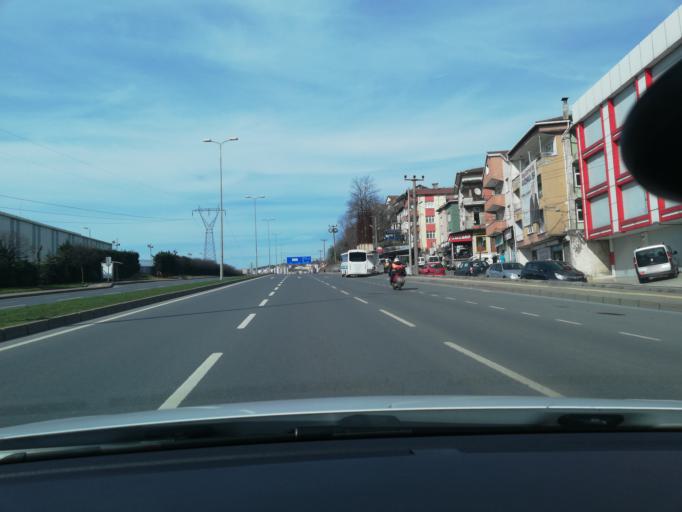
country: TR
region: Zonguldak
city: Eregli
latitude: 41.2629
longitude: 31.4353
